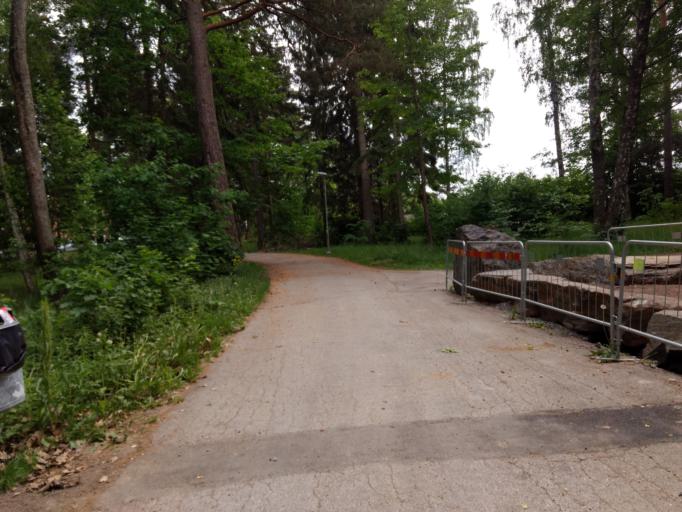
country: SE
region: Stockholm
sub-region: Upplands Vasby Kommun
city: Upplands Vaesby
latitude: 59.5269
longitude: 17.9114
